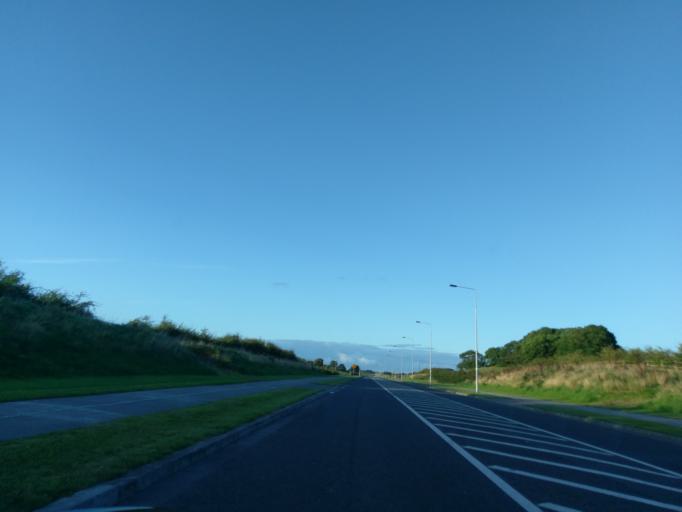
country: IE
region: Connaught
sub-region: County Galway
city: Athenry
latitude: 53.3053
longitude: -8.7648
